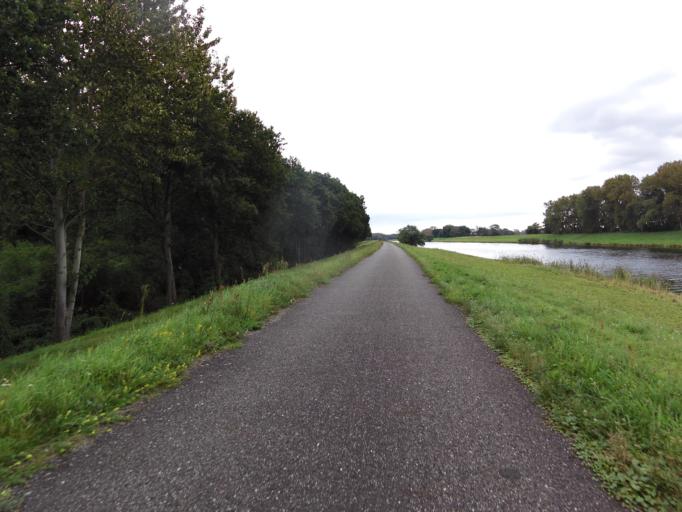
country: DE
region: Brandenburg
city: Bad Wilsnack
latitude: 52.8939
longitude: 11.9376
